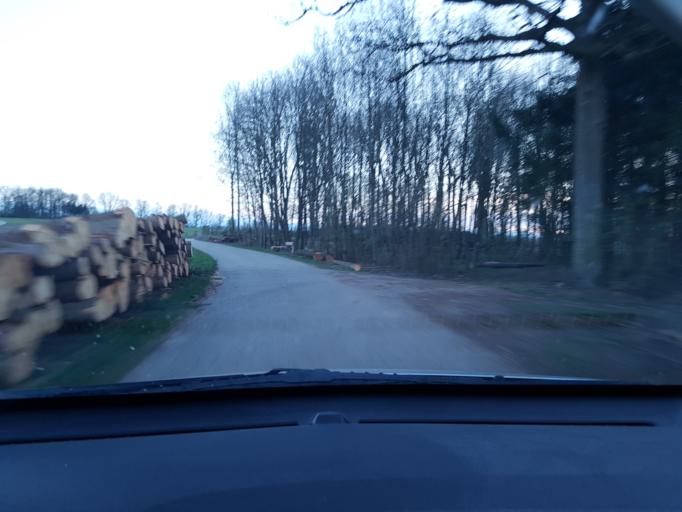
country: AT
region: Upper Austria
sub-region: Politischer Bezirk Linz-Land
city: Ansfelden
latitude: 48.1775
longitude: 14.3207
